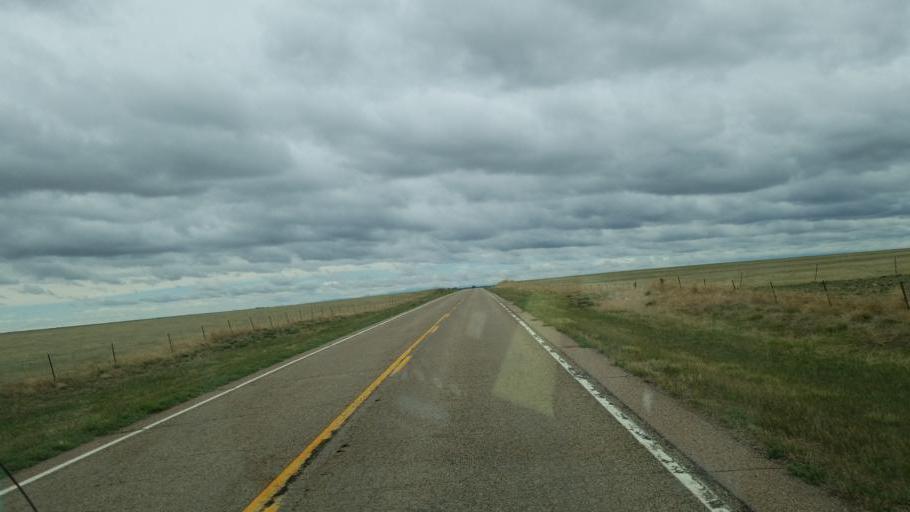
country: US
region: Colorado
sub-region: El Paso County
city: Ellicott
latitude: 38.8394
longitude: -103.9152
